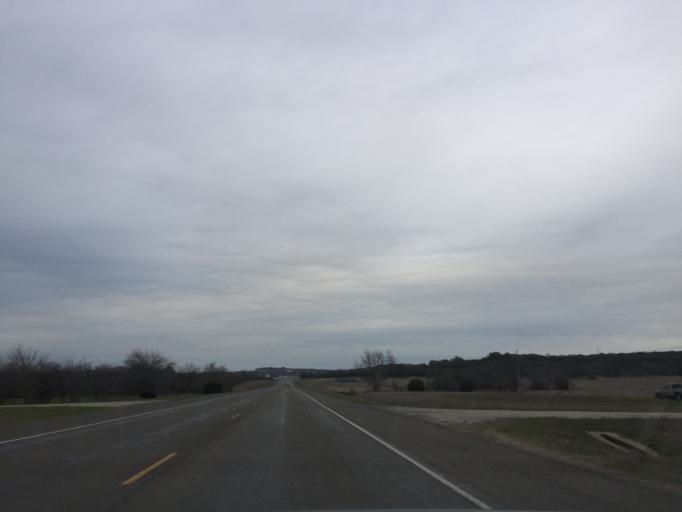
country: US
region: Texas
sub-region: Coryell County
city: Gatesville
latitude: 31.4564
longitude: -97.7161
